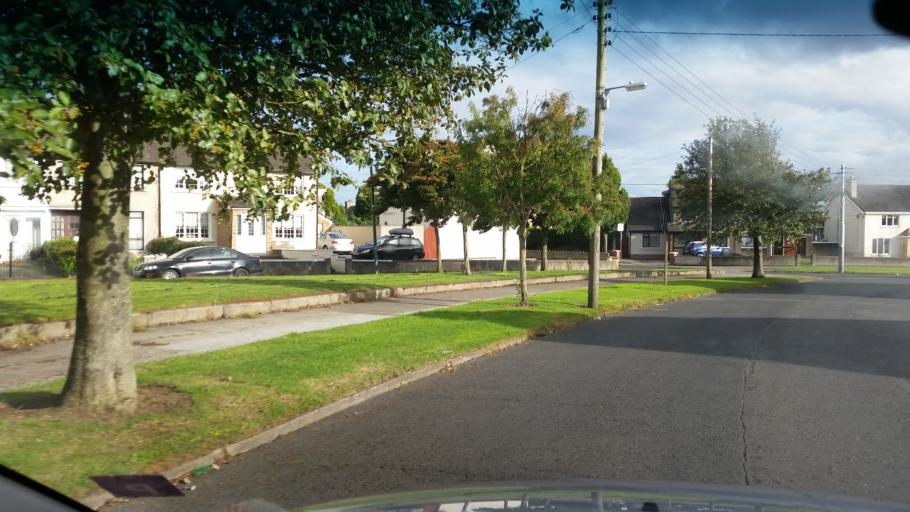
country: IE
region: Leinster
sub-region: Dublin City
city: Finglas
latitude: 53.3825
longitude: -6.2832
